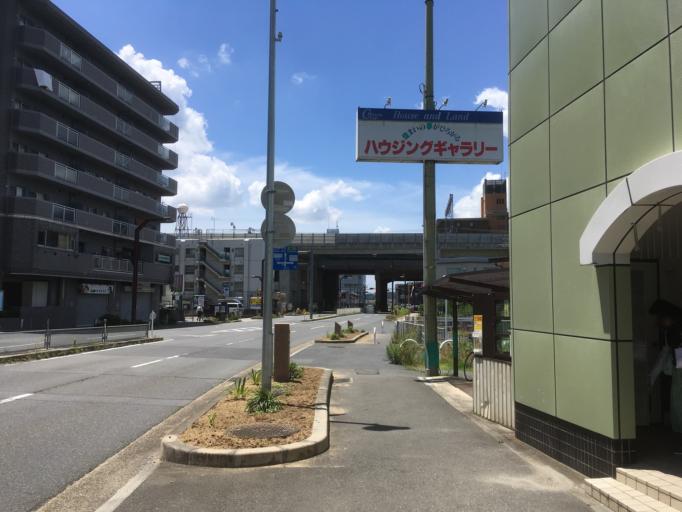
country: JP
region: Nara
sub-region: Ikoma-shi
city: Ikoma
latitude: 34.6933
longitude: 135.7094
